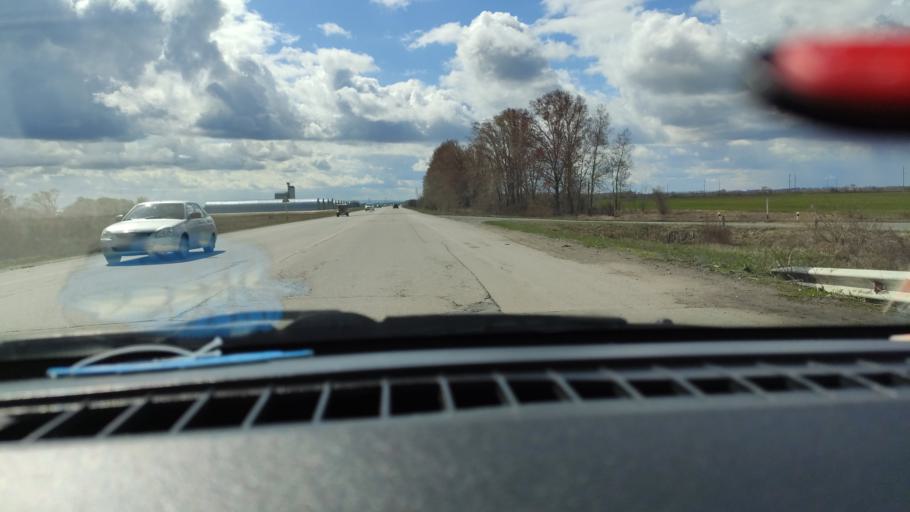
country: RU
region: Samara
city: Tol'yatti
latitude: 53.6892
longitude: 49.4179
